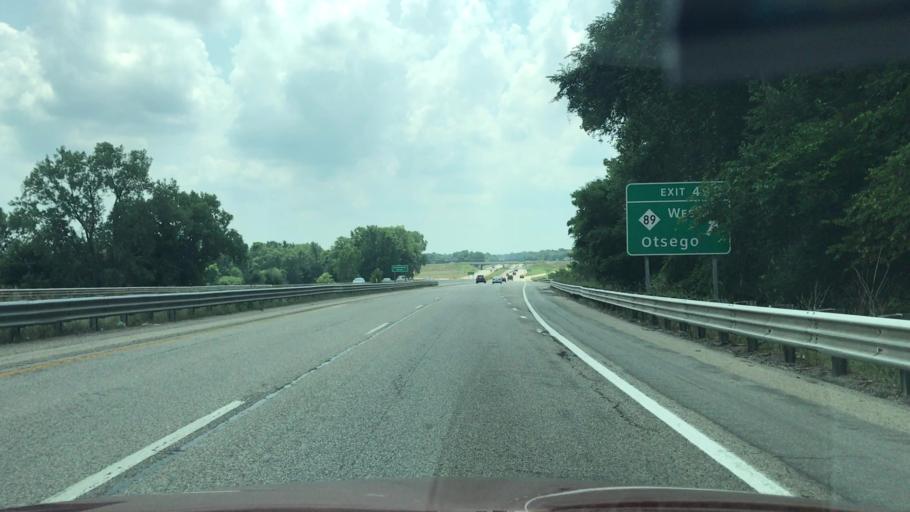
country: US
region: Michigan
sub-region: Allegan County
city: Plainwell
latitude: 42.4570
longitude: -85.6531
